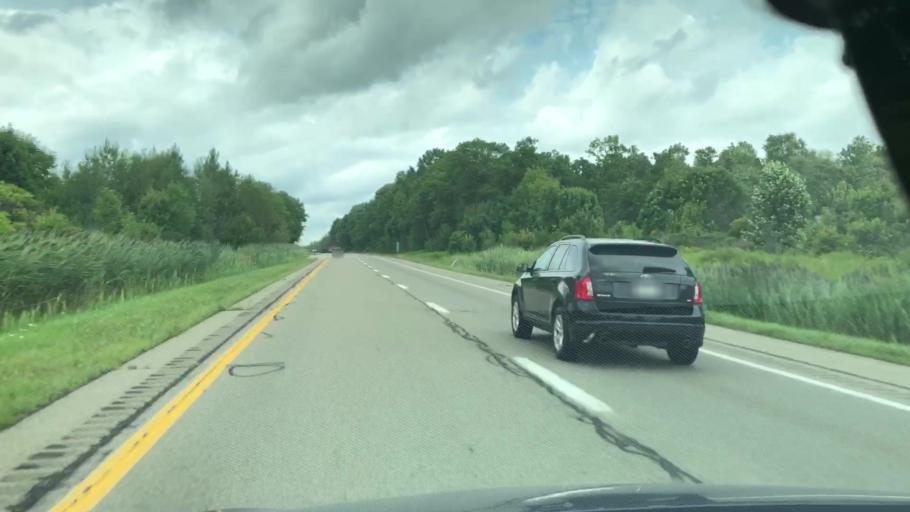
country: US
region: Pennsylvania
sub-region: Erie County
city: Edinboro
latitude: 41.8258
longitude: -80.1748
